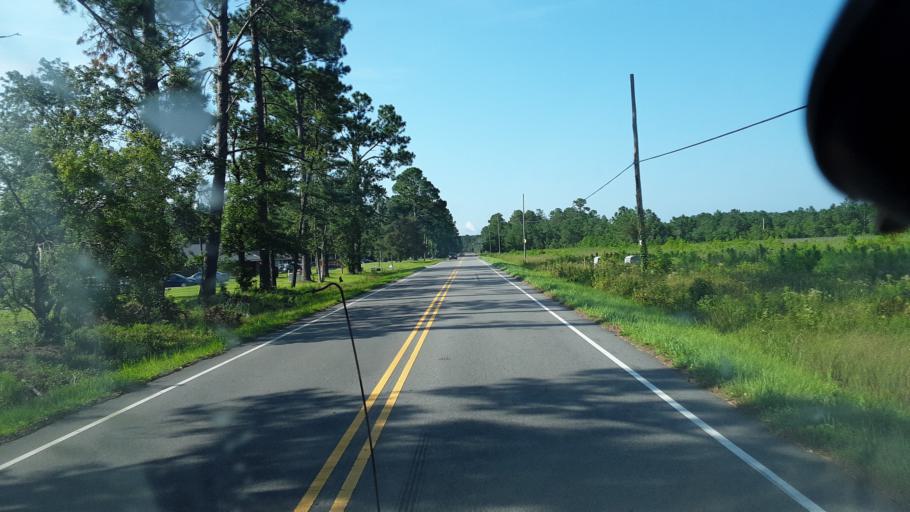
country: US
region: North Carolina
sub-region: Brunswick County
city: Belville
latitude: 34.1876
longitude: -77.9879
